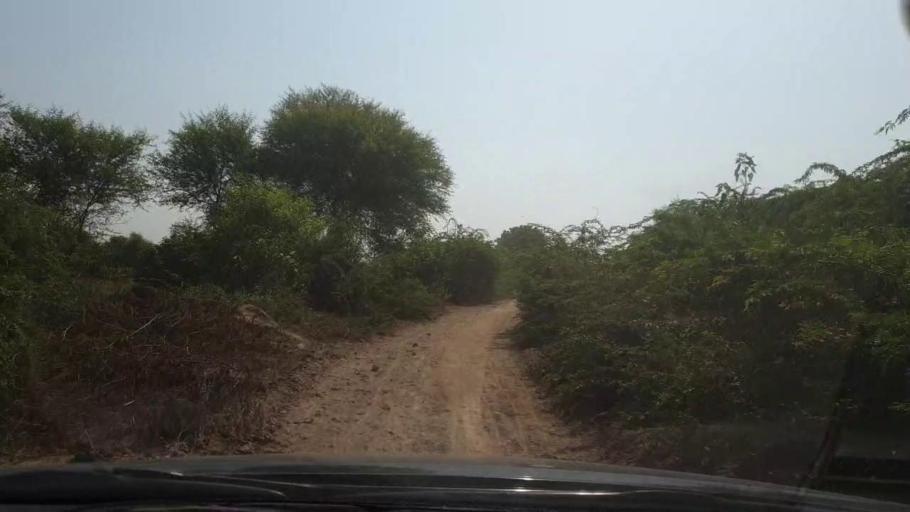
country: PK
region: Sindh
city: Naukot
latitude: 24.8091
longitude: 69.2605
